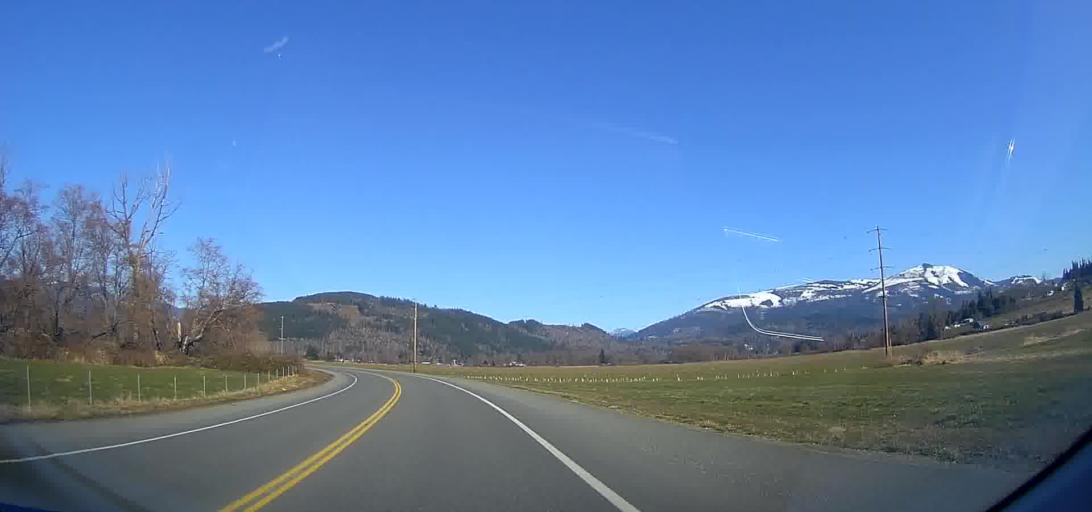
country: US
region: Washington
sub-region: Skagit County
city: Clear Lake
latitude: 48.4646
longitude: -122.2588
